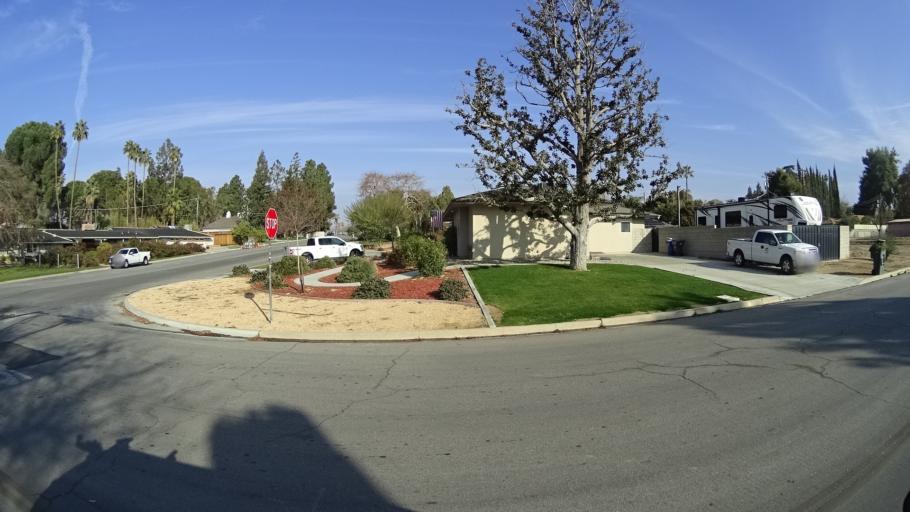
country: US
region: California
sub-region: Kern County
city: Oildale
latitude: 35.4048
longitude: -118.9940
